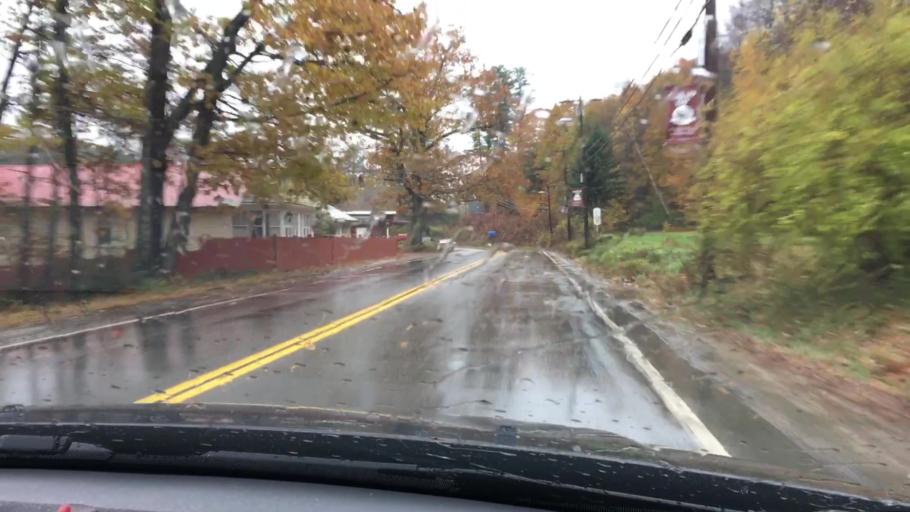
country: US
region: New Hampshire
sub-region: Grafton County
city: Ashland
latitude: 43.7022
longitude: -71.6305
